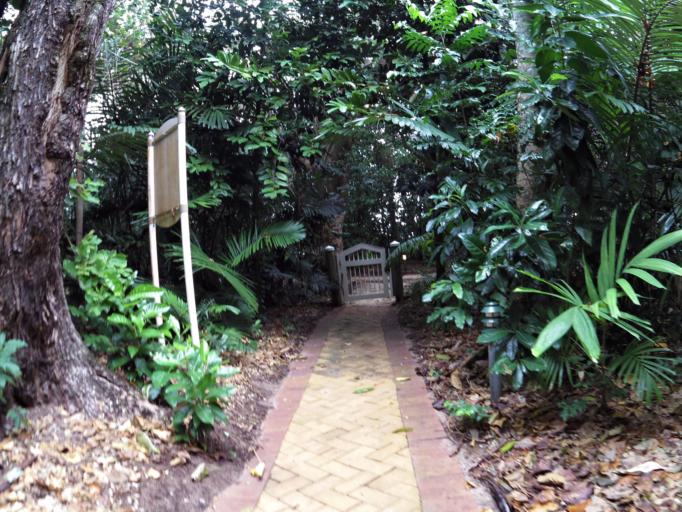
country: AU
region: Queensland
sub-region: Cairns
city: Yorkeys Knob
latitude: -16.7598
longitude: 145.9720
